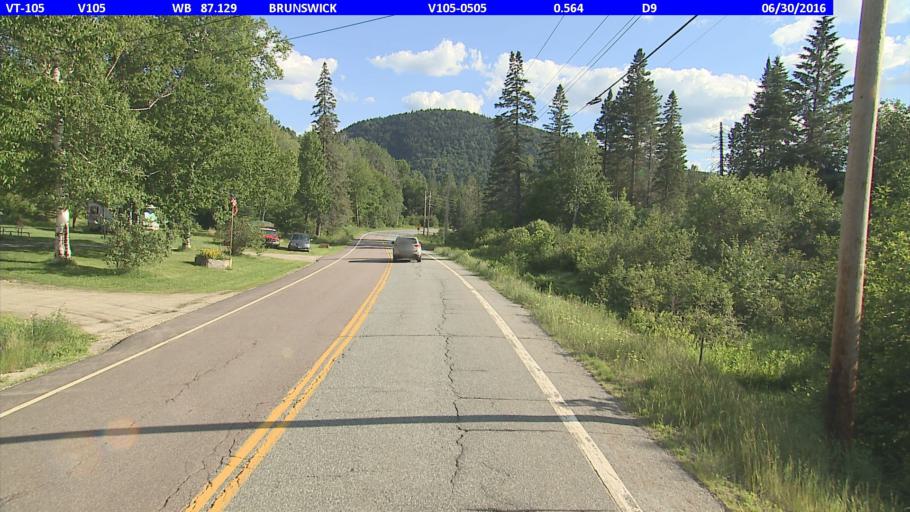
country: US
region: New Hampshire
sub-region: Coos County
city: Stratford
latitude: 44.7639
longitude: -71.7106
